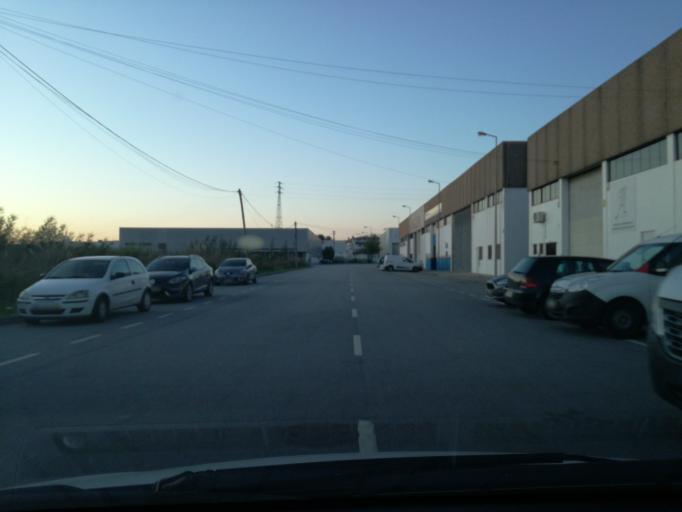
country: PT
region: Porto
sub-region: Maia
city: Gemunde
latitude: 41.2553
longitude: -8.6409
